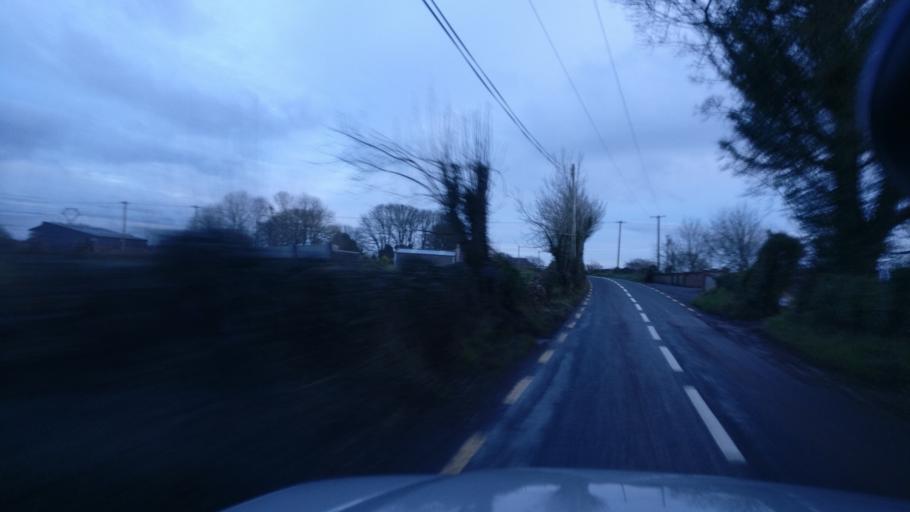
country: IE
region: Connaught
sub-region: County Galway
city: Athenry
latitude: 53.2538
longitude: -8.6760
